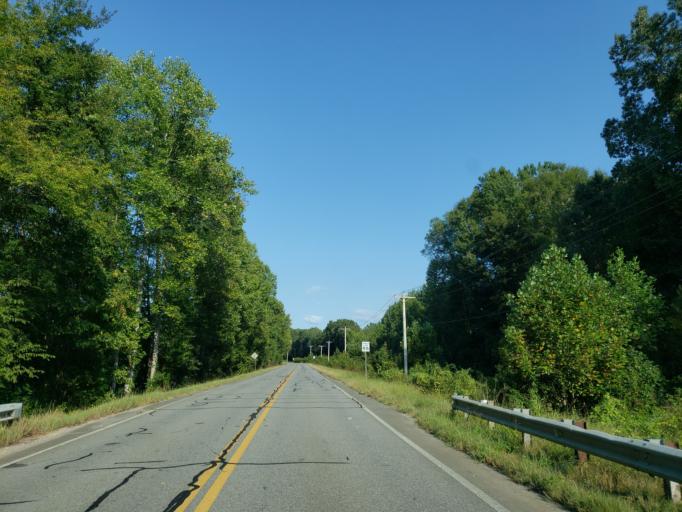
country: US
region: Georgia
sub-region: Whitfield County
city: Varnell
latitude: 34.9214
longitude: -84.8341
